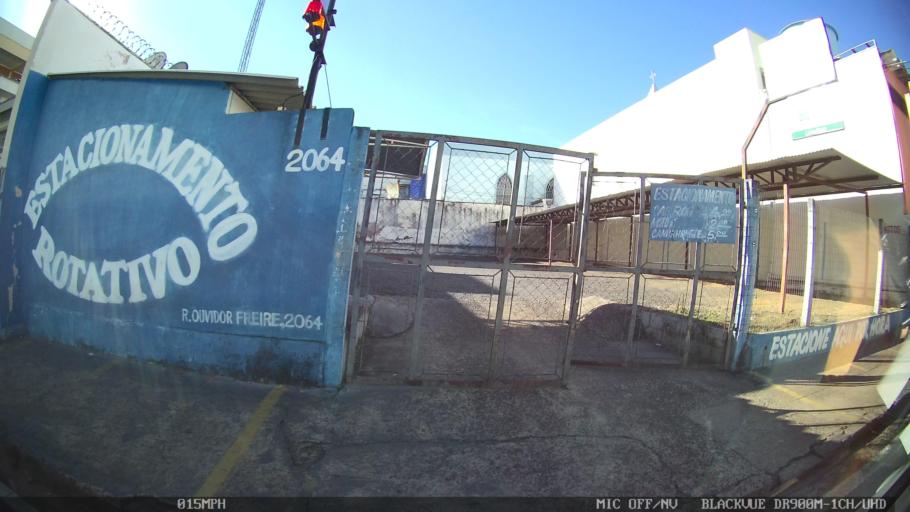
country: BR
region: Sao Paulo
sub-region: Franca
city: Franca
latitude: -20.5355
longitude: -47.4025
